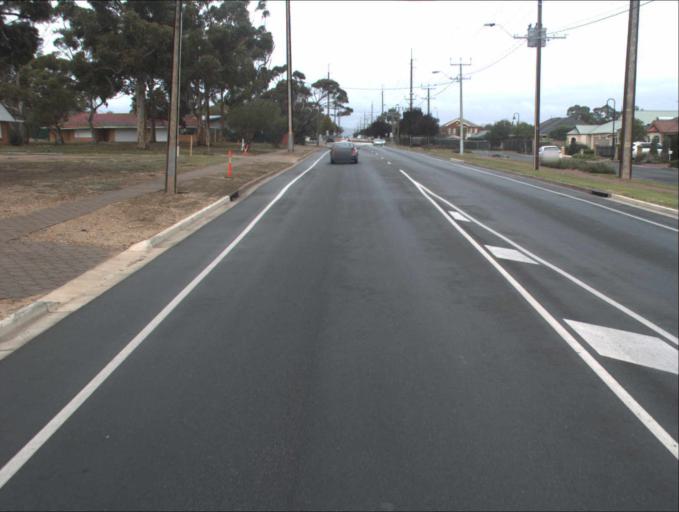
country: AU
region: South Australia
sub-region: Port Adelaide Enfield
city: Gilles Plains
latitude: -34.8494
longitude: 138.6355
